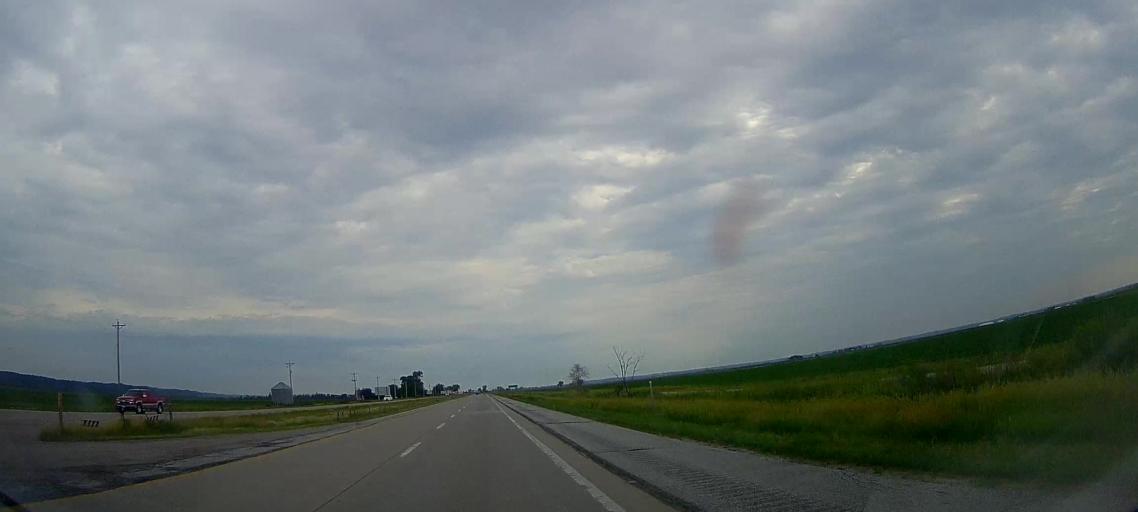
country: US
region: Iowa
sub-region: Harrison County
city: Missouri Valley
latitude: 41.5407
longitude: -95.9178
